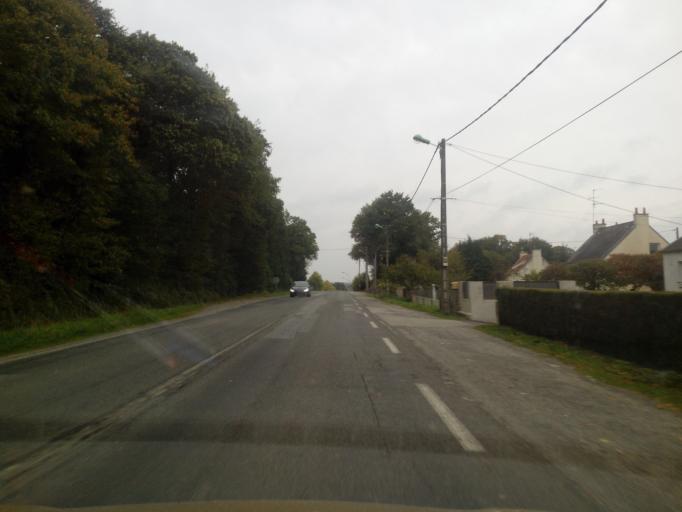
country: FR
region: Brittany
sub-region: Departement du Morbihan
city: Hennebont
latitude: 47.7987
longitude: -3.2541
